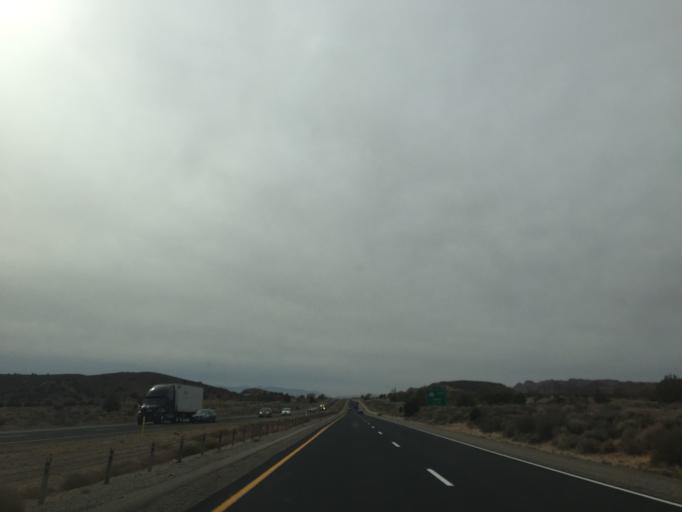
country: US
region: Utah
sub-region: Washington County
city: Toquerville
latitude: 37.2523
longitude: -113.3408
